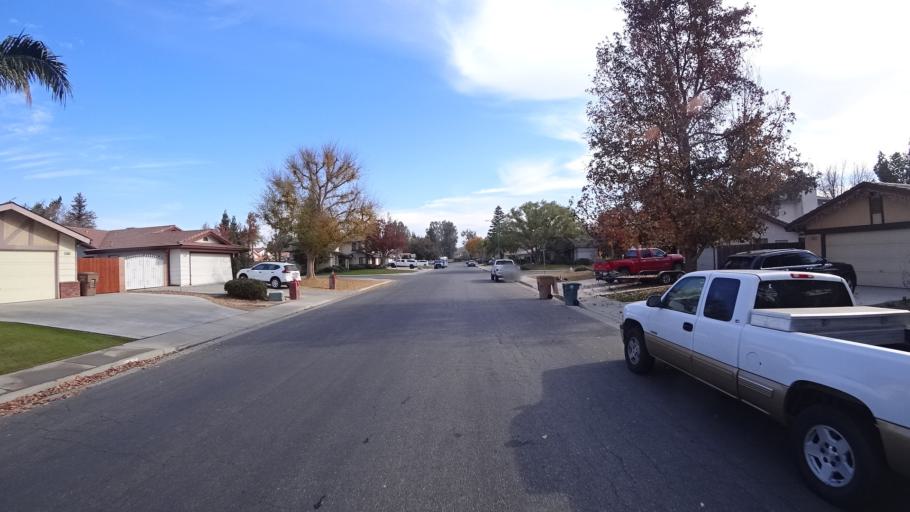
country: US
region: California
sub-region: Kern County
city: Greenacres
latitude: 35.4038
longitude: -119.0786
